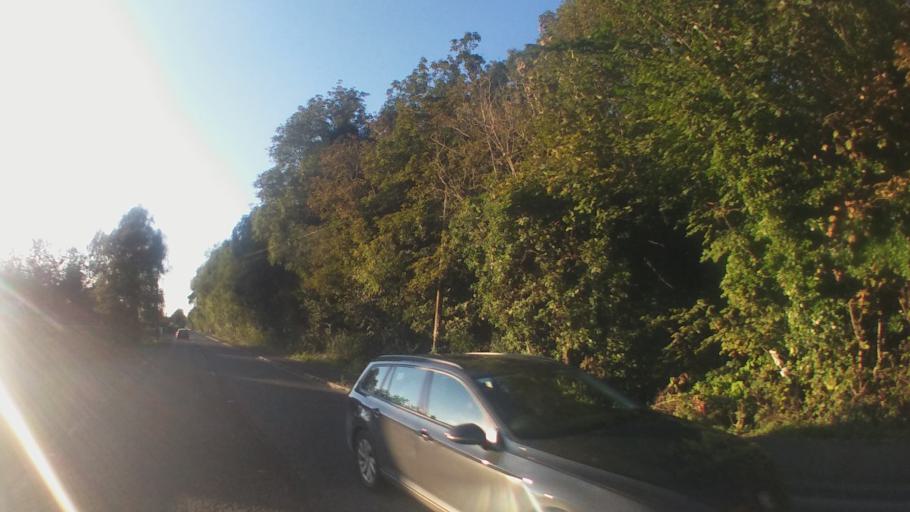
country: IE
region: Leinster
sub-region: Lu
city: Blackrock
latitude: 54.0191
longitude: -6.3299
